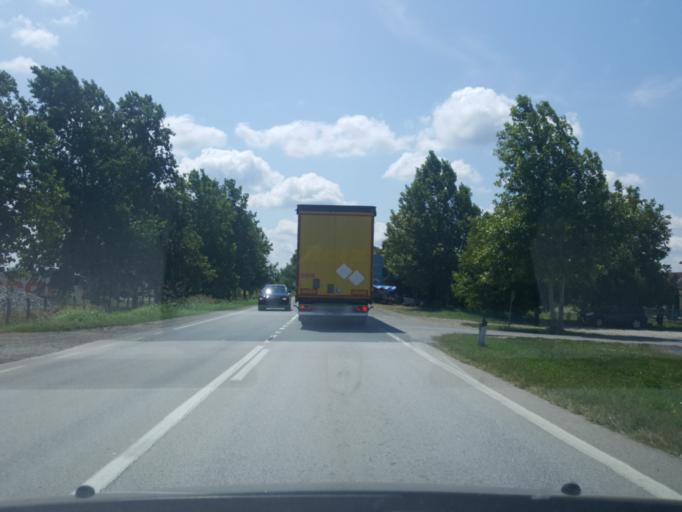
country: RS
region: Autonomna Pokrajina Vojvodina
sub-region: Sremski Okrug
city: Sremska Mitrovica
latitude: 44.9815
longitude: 19.6390
